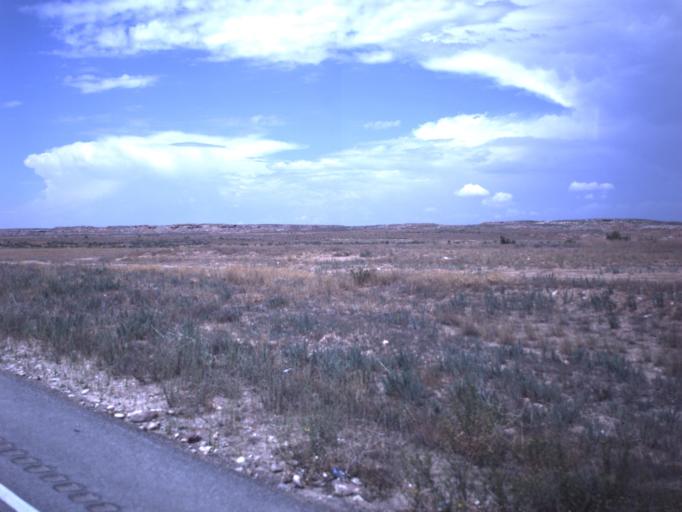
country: US
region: Utah
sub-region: Uintah County
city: Maeser
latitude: 40.3345
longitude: -109.6442
